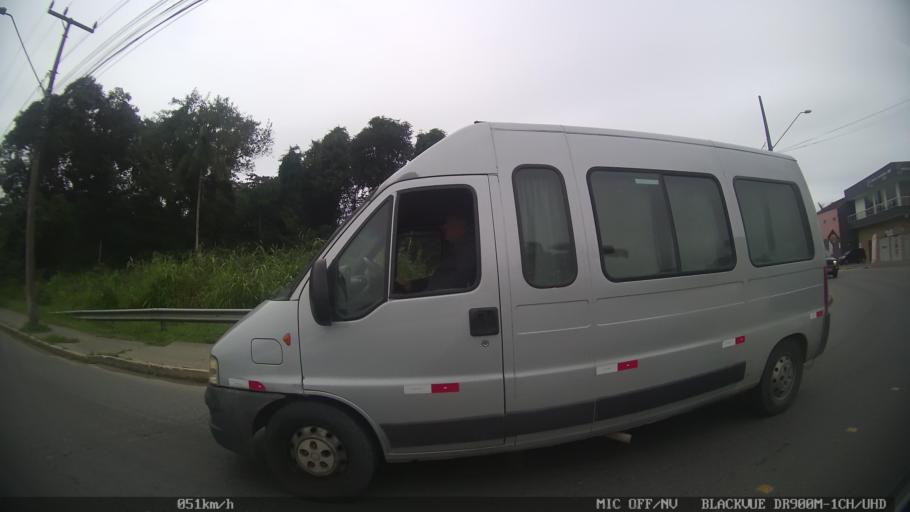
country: BR
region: Santa Catarina
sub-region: Joinville
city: Joinville
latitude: -26.2906
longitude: -48.8919
